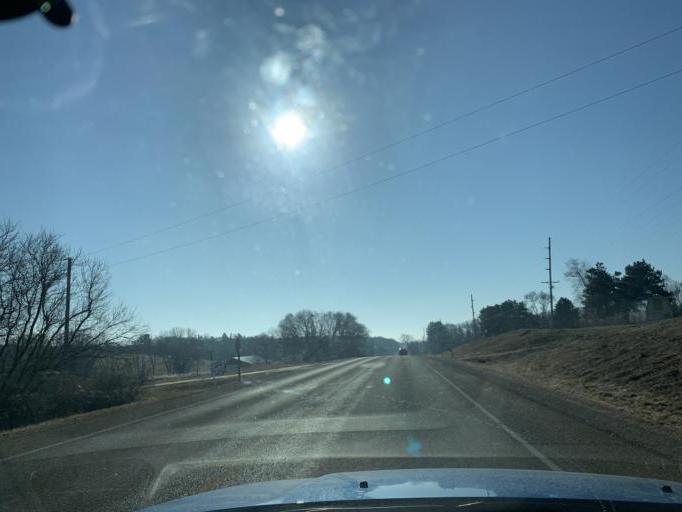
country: US
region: Wisconsin
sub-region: Dane County
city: Verona
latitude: 42.9569
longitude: -89.5145
